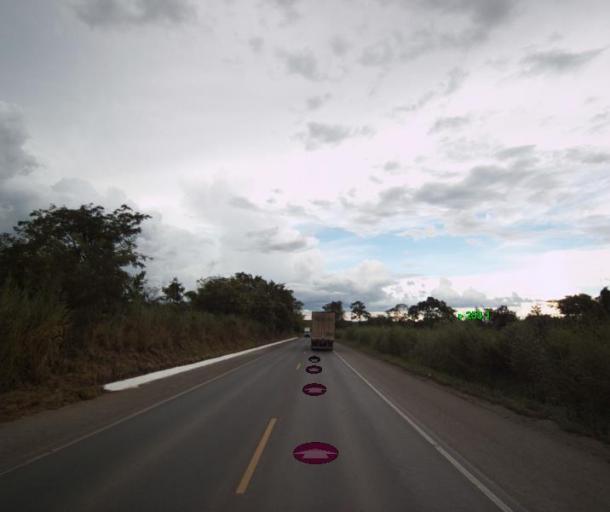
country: BR
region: Goias
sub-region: Itapaci
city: Itapaci
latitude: -14.9456
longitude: -49.3744
